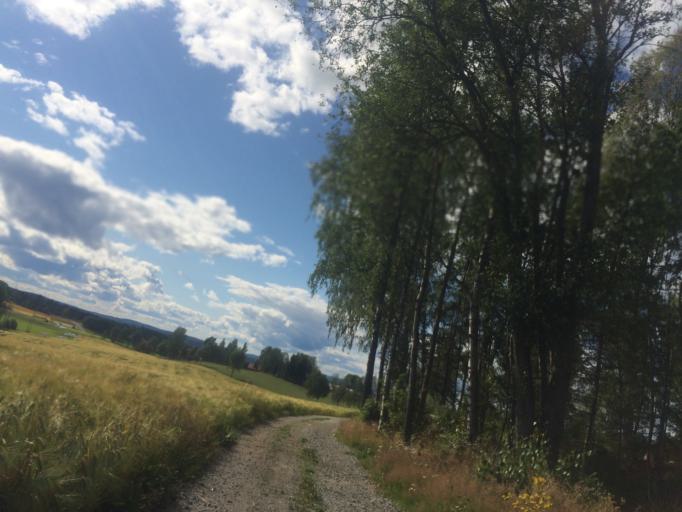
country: NO
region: Akershus
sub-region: As
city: As
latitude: 59.6738
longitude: 10.7883
